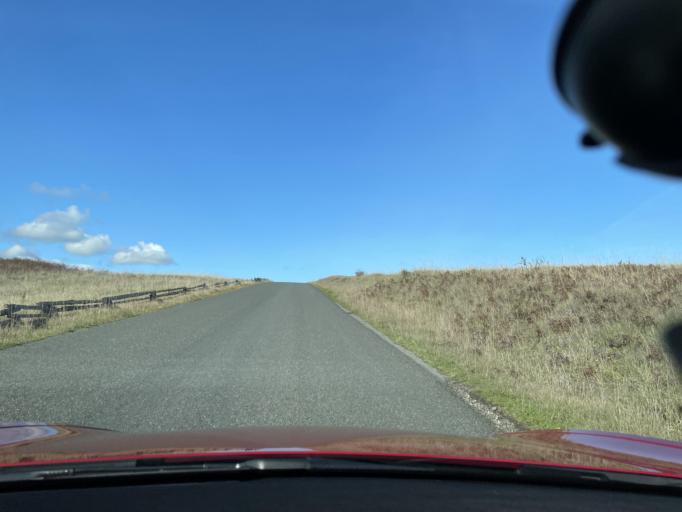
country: US
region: Washington
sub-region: San Juan County
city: Friday Harbor
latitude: 48.4572
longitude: -123.0016
